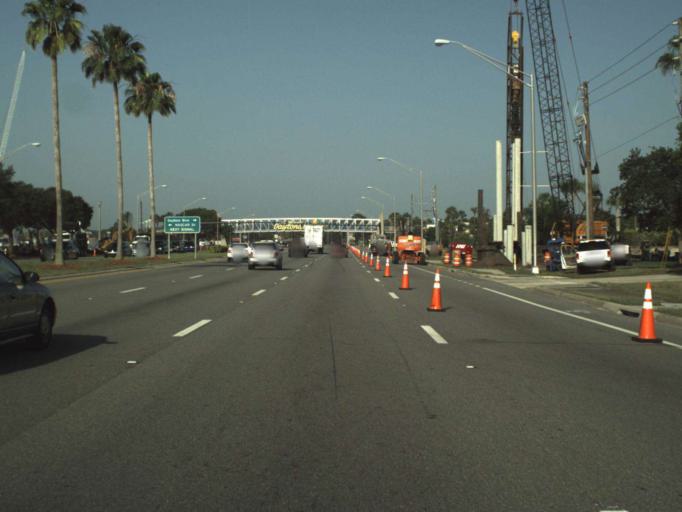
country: US
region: Florida
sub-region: Volusia County
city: Daytona Beach
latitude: 29.1926
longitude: -81.0683
